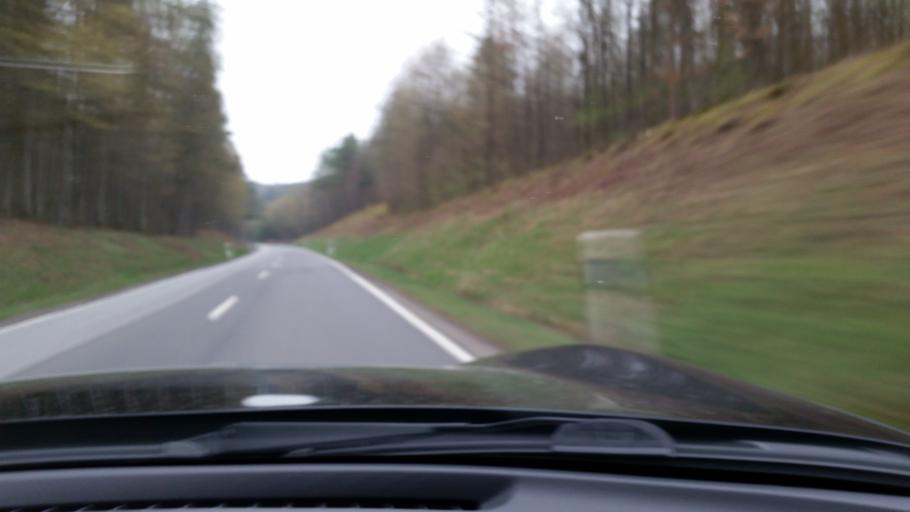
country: DE
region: Baden-Wuerttemberg
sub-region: Karlsruhe Region
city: Osterburken
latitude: 49.4586
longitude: 9.4171
